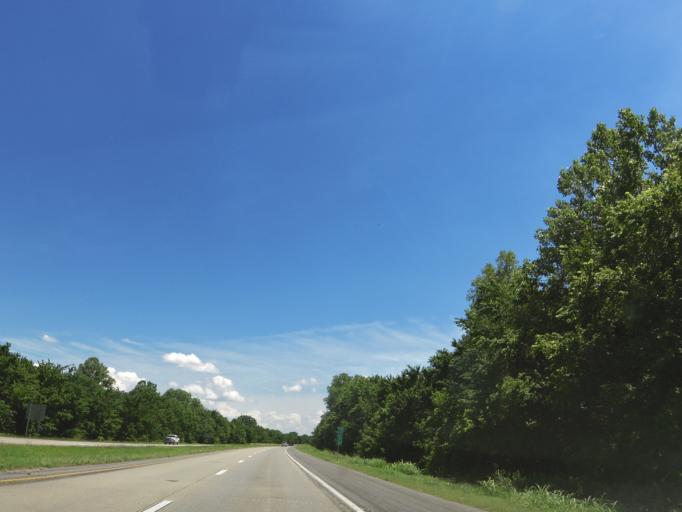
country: US
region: Missouri
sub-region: Pemiscot County
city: Caruthersville
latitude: 36.1343
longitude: -89.6273
